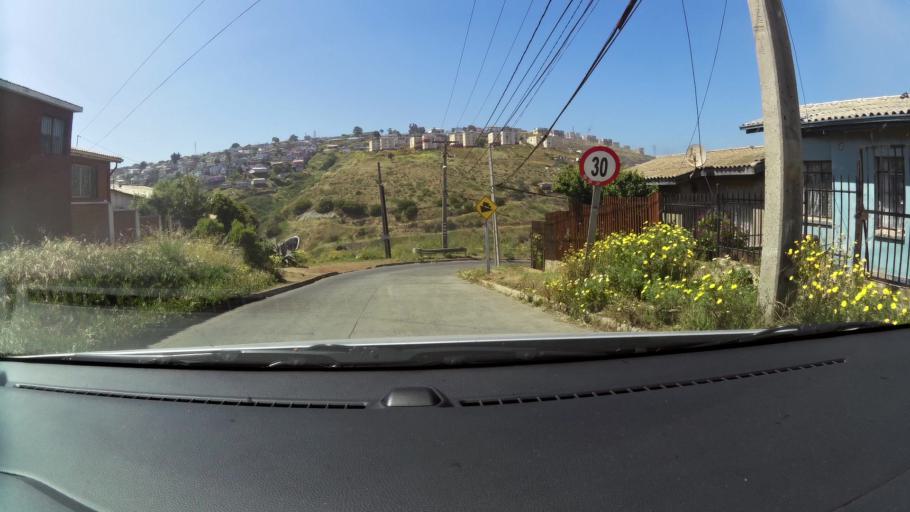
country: CL
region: Valparaiso
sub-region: Provincia de Valparaiso
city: Valparaiso
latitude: -33.0411
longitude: -71.6549
